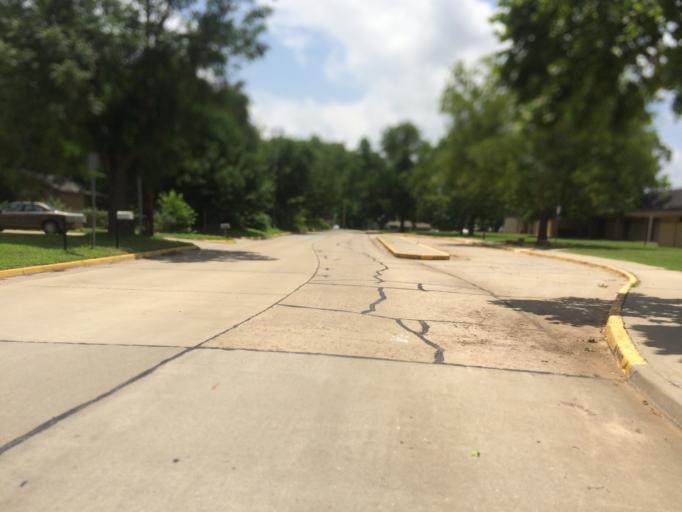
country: US
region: Oklahoma
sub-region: Cleveland County
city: Norman
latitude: 35.2127
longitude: -97.4690
